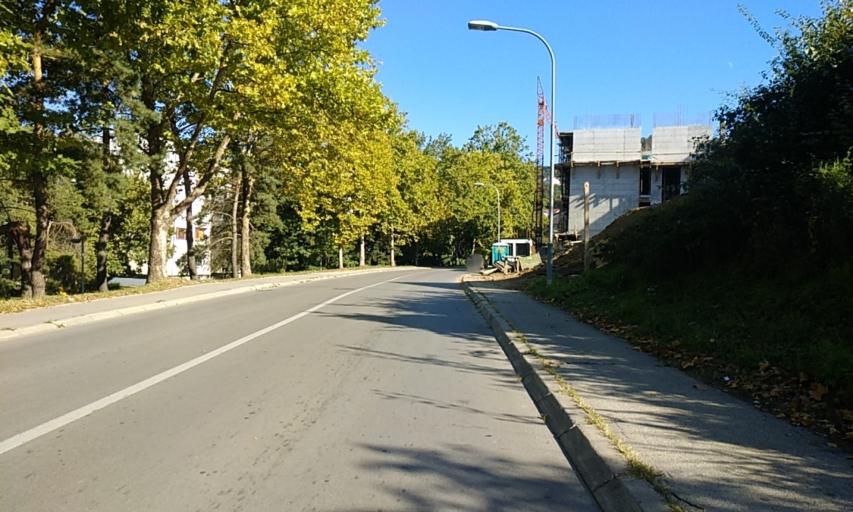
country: BA
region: Republika Srpska
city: Starcevica
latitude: 44.7585
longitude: 17.2051
